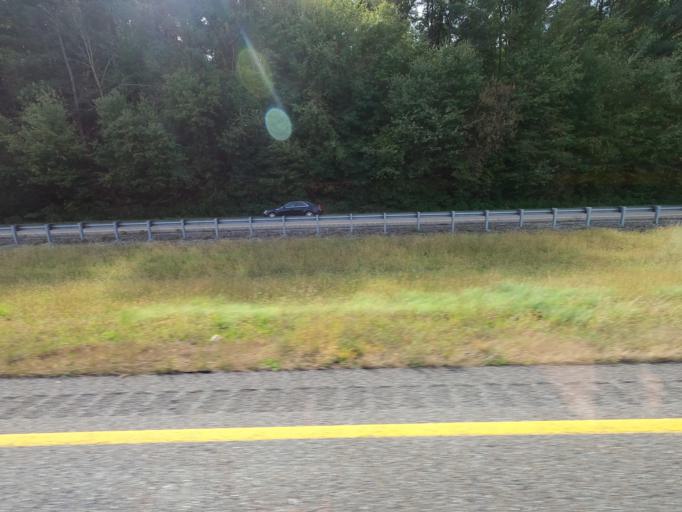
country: US
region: Tennessee
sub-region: Humphreys County
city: New Johnsonville
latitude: 35.8668
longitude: -87.9217
